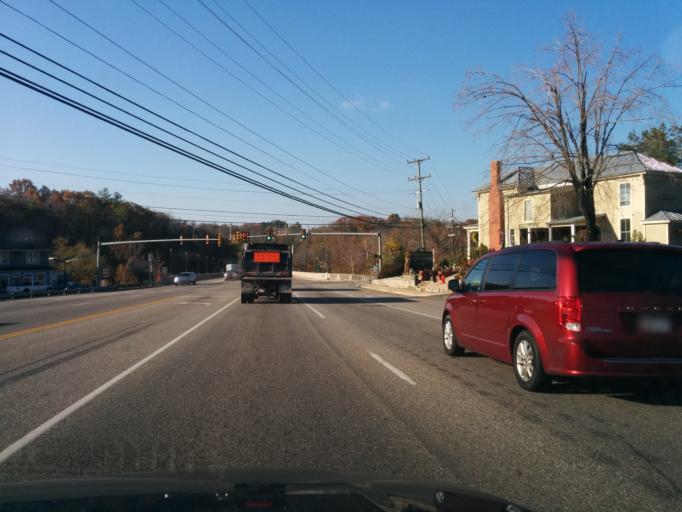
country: US
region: Virginia
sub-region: Rockbridge County
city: East Lexington
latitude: 37.7935
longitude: -79.4254
